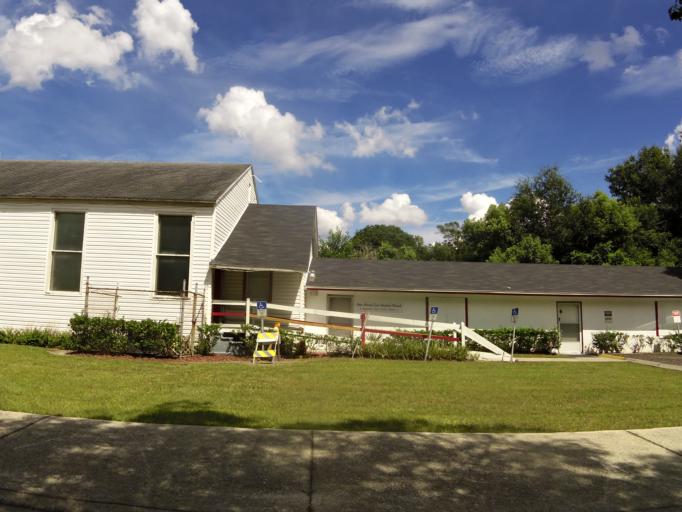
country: US
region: Florida
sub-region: Duval County
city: Jacksonville
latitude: 30.3852
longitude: -81.6416
